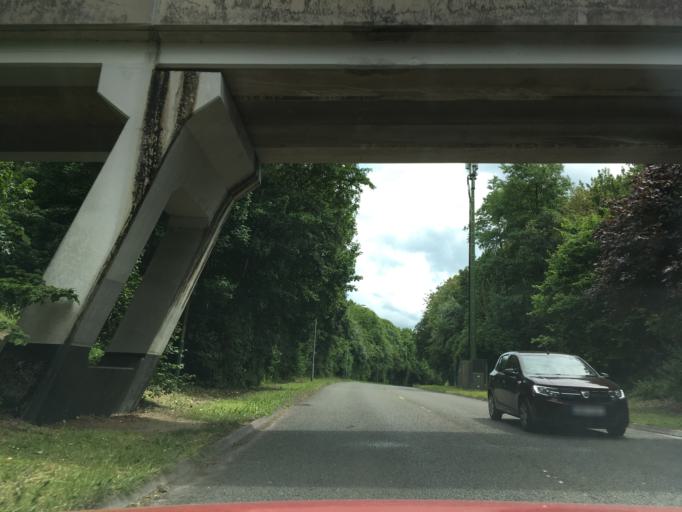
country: GB
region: England
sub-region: Wiltshire
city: Lydiard Tregoze
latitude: 51.5617
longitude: -1.8368
